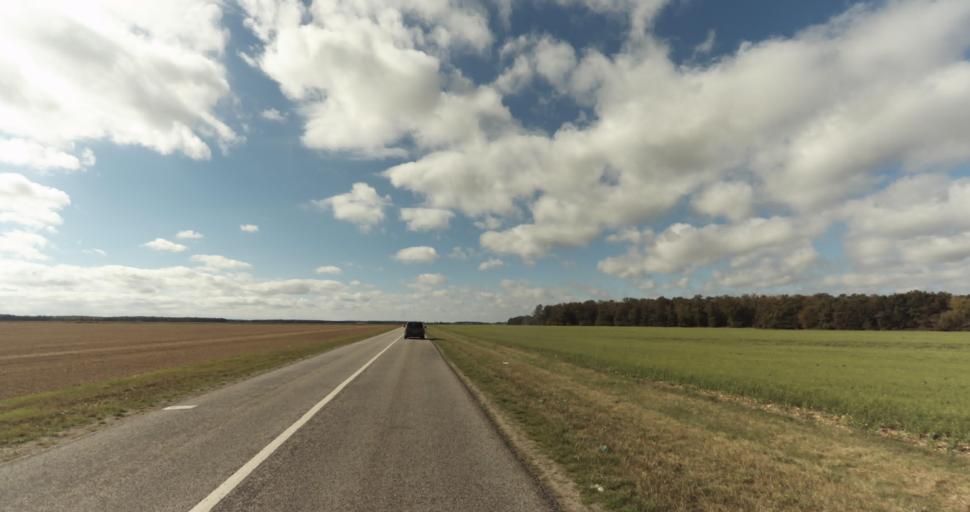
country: FR
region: Centre
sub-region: Departement d'Eure-et-Loir
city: Garnay
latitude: 48.7197
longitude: 1.3211
